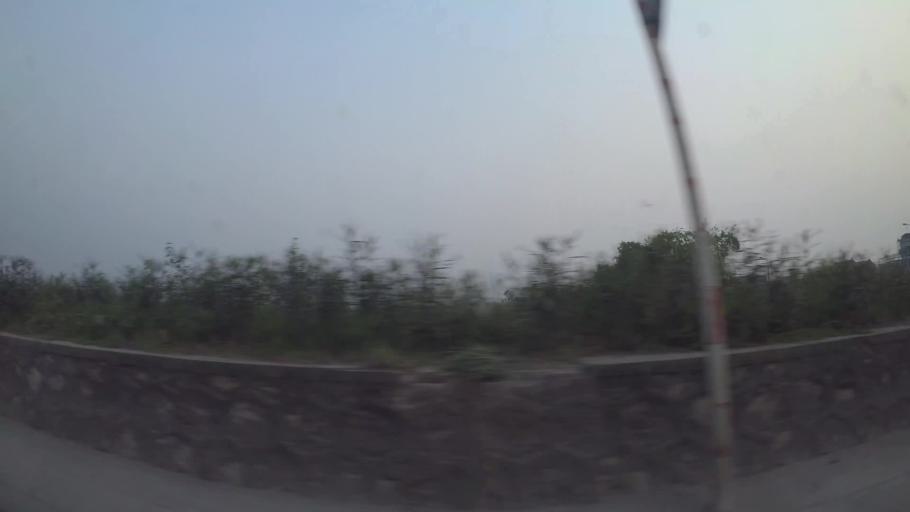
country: VN
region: Ha Noi
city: Van Dien
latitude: 20.9718
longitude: 105.8853
